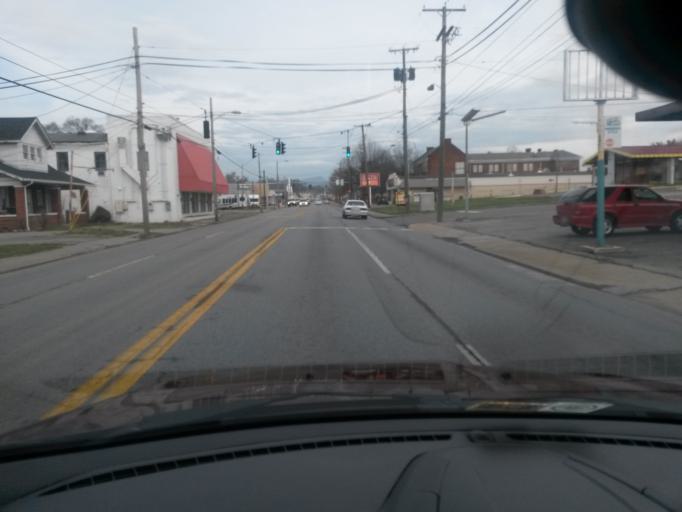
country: US
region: Virginia
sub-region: City of Roanoke
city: Roanoke
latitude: 37.2999
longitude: -79.9412
